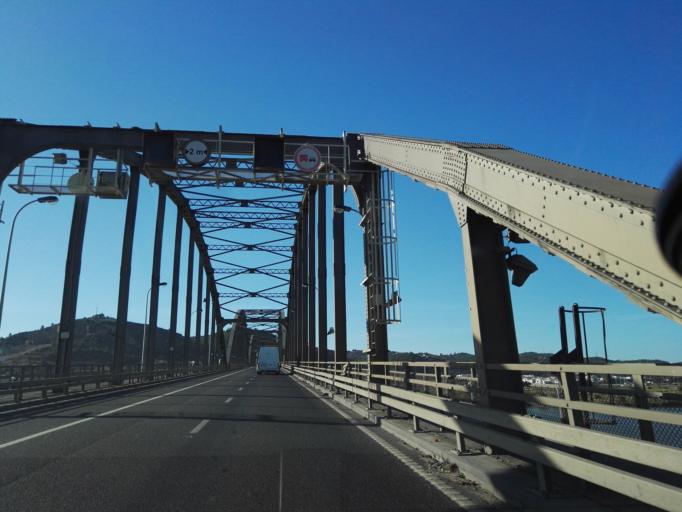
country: PT
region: Lisbon
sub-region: Vila Franca de Xira
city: Vila Franca de Xira
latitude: 38.9547
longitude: -8.9767
